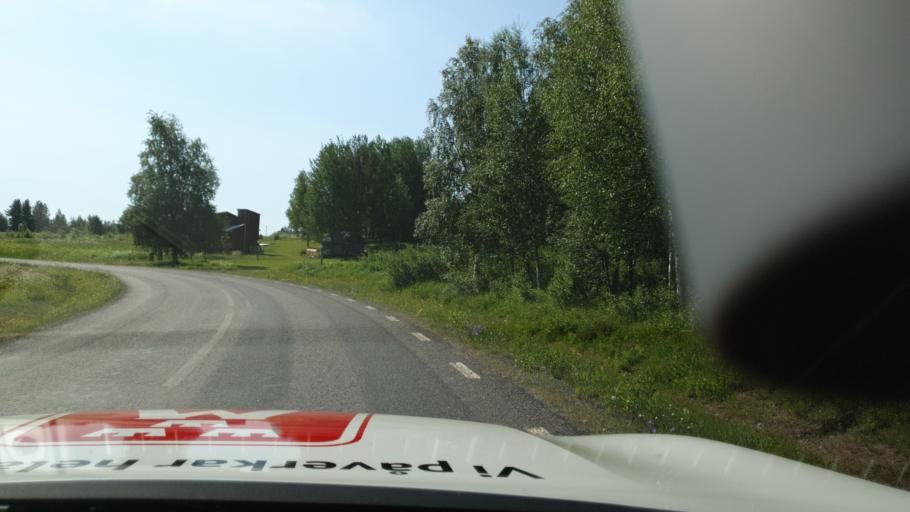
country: SE
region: Vaesterbotten
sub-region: Skelleftea Kommun
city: Langsele
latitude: 65.0071
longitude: 20.0881
